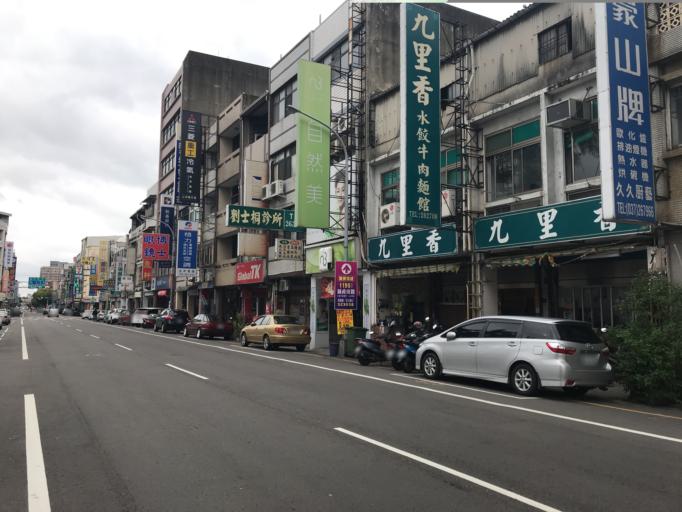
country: TW
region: Taiwan
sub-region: Miaoli
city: Miaoli
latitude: 24.5675
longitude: 120.8243
